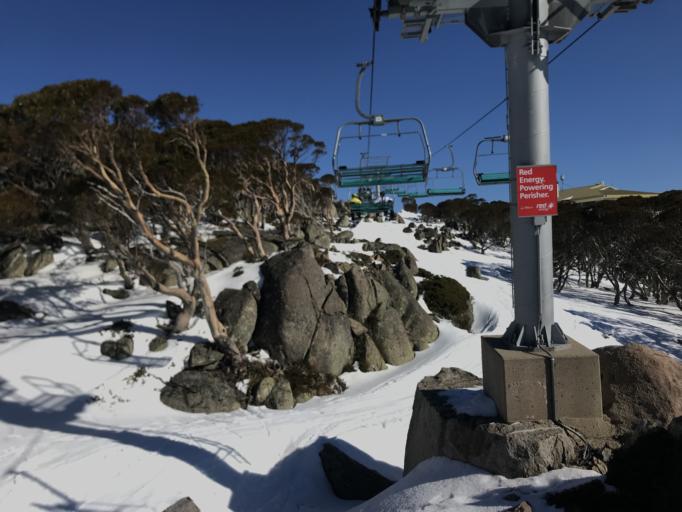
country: AU
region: New South Wales
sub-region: Snowy River
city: Jindabyne
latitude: -36.3851
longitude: 148.3951
